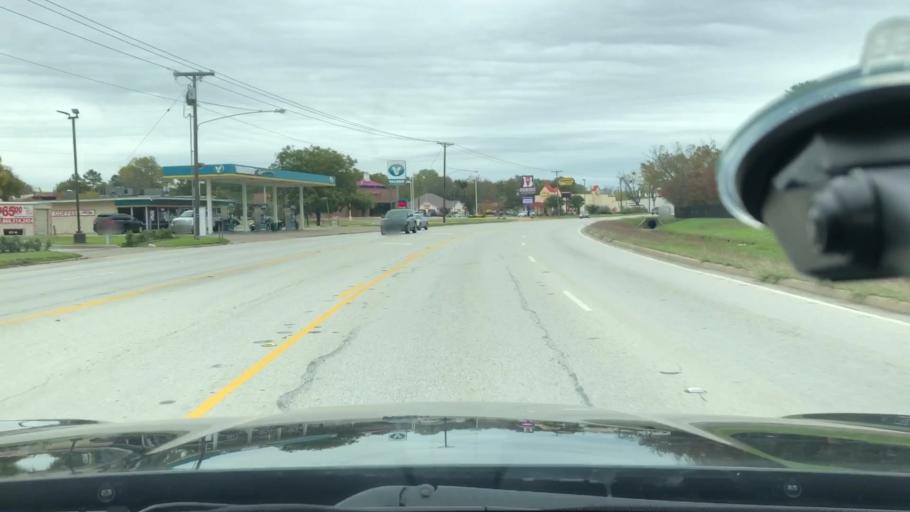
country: US
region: Texas
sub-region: Kaufman County
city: Terrell
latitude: 32.7390
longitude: -96.2924
